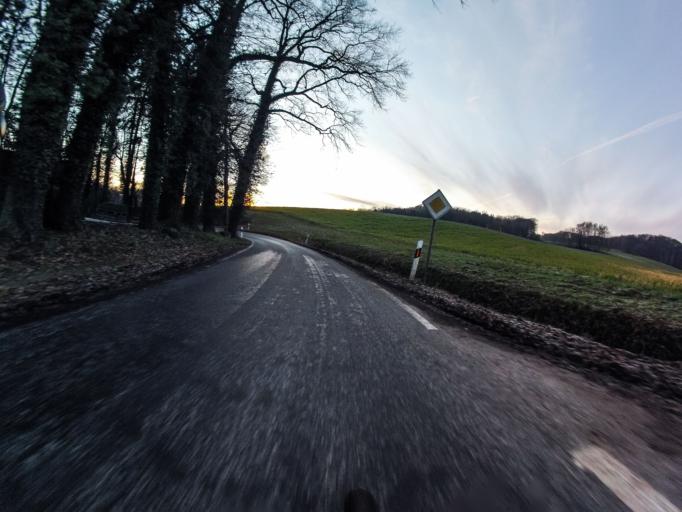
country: DE
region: North Rhine-Westphalia
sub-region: Regierungsbezirk Munster
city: Tecklenburg
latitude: 52.2655
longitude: 7.8360
